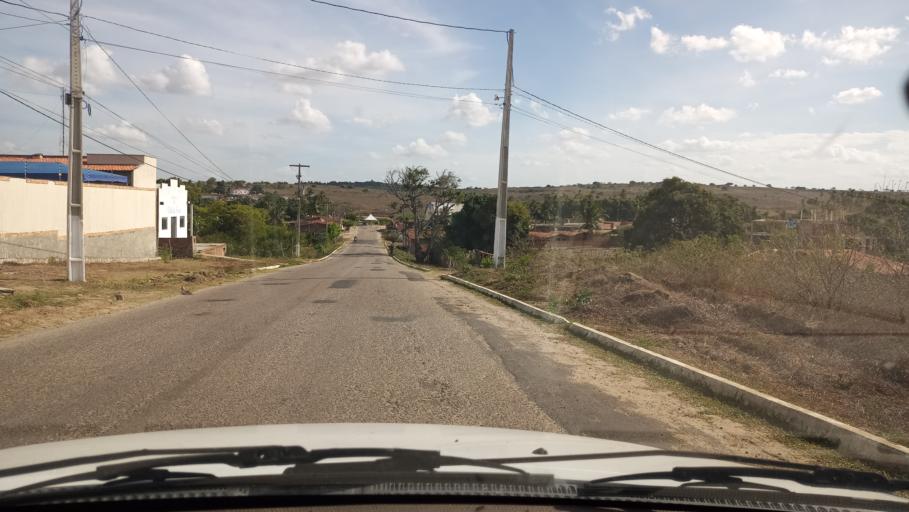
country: BR
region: Rio Grande do Norte
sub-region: Goianinha
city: Goianinha
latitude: -6.3281
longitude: -35.3043
